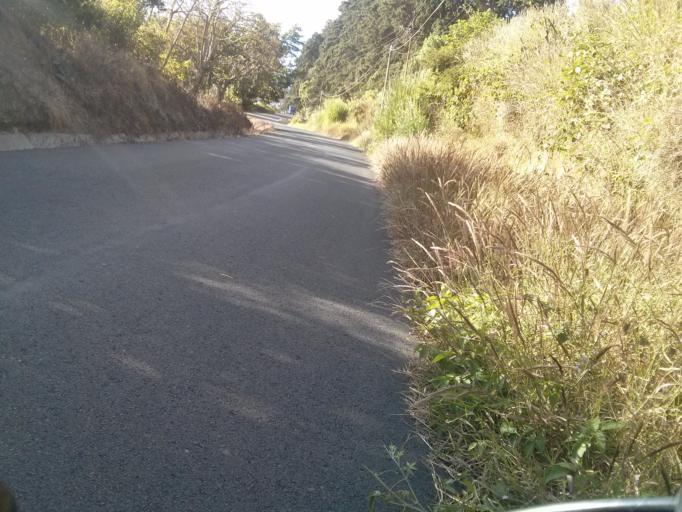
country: CR
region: Cartago
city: Tres Rios
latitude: 9.9174
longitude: -83.9547
